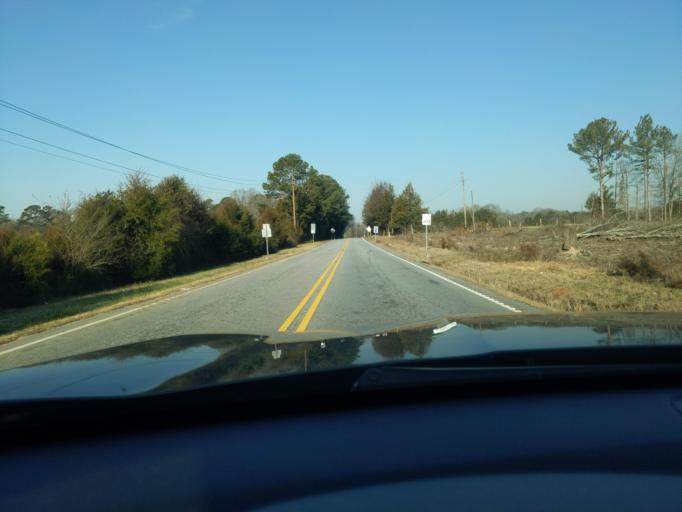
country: US
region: South Carolina
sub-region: Greenwood County
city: Ninety Six
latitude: 34.1710
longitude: -82.0808
